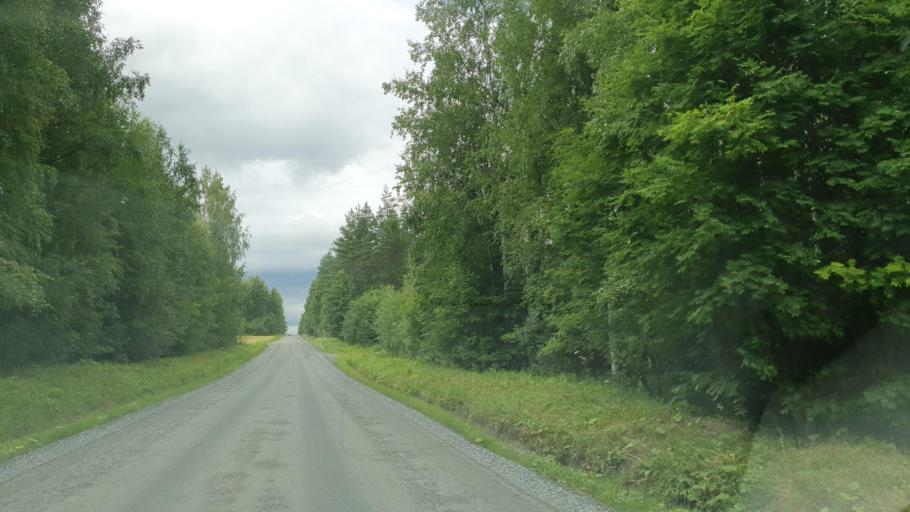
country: FI
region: Northern Savo
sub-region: Ylae-Savo
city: Iisalmi
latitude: 63.5208
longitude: 27.0979
